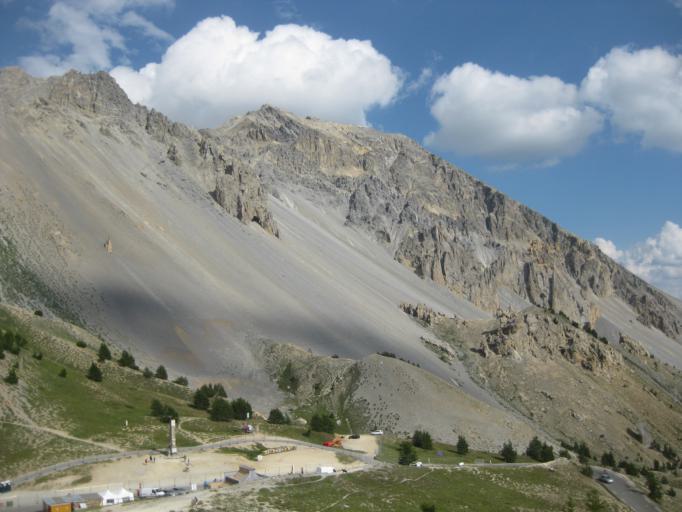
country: FR
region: Provence-Alpes-Cote d'Azur
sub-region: Departement des Hautes-Alpes
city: Villar-Saint-Pancrace
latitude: 44.8203
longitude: 6.7331
